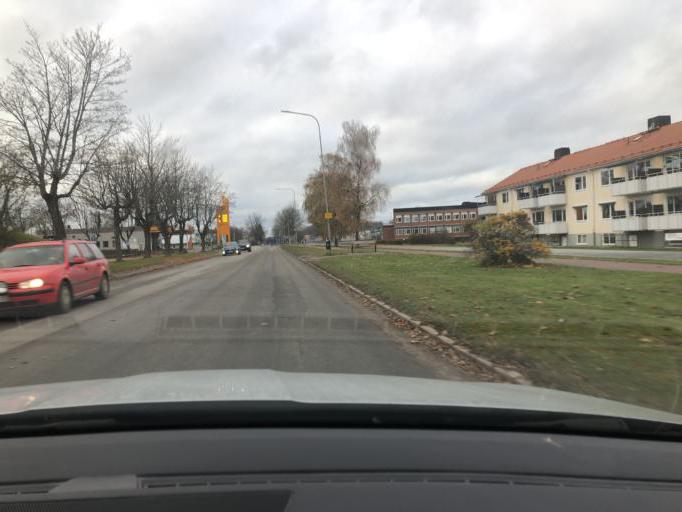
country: SE
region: Uppsala
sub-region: Tierps Kommun
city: Tierp
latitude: 60.3437
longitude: 17.5086
